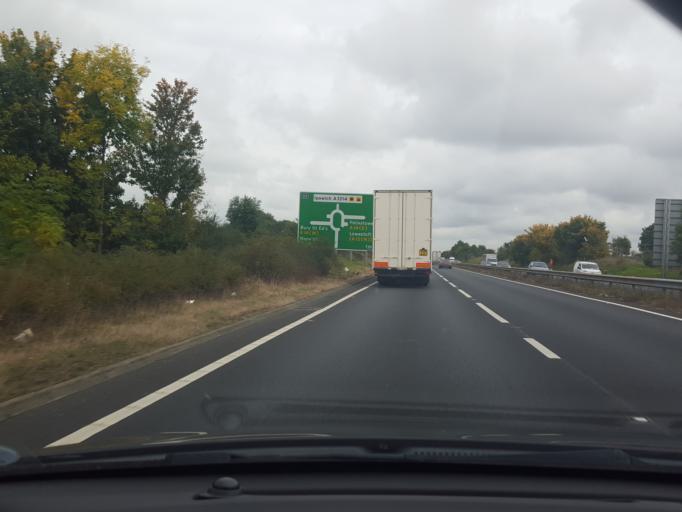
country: GB
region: England
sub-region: Suffolk
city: Capel Saint Mary
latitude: 52.0230
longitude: 1.0846
